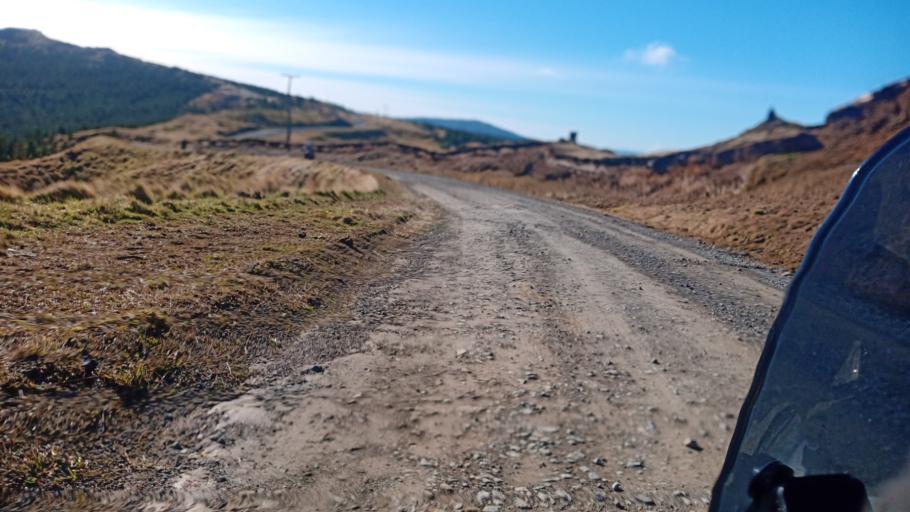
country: NZ
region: Gisborne
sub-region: Gisborne District
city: Gisborne
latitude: -38.1948
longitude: 177.8111
